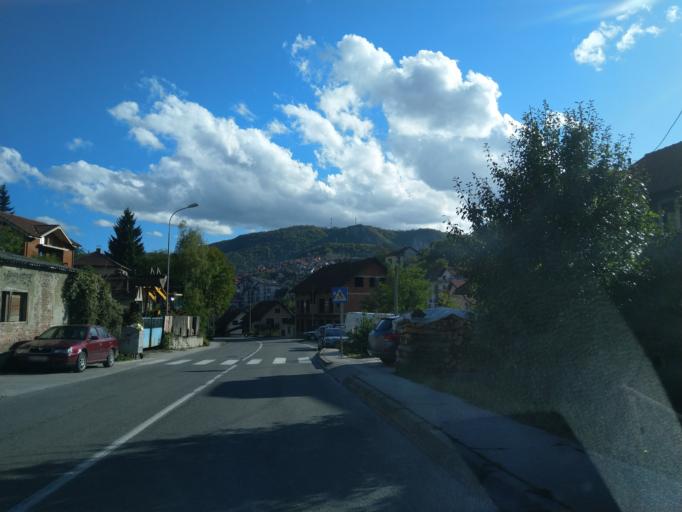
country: RS
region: Central Serbia
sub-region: Zlatiborski Okrug
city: Uzice
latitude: 43.8626
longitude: 19.8254
